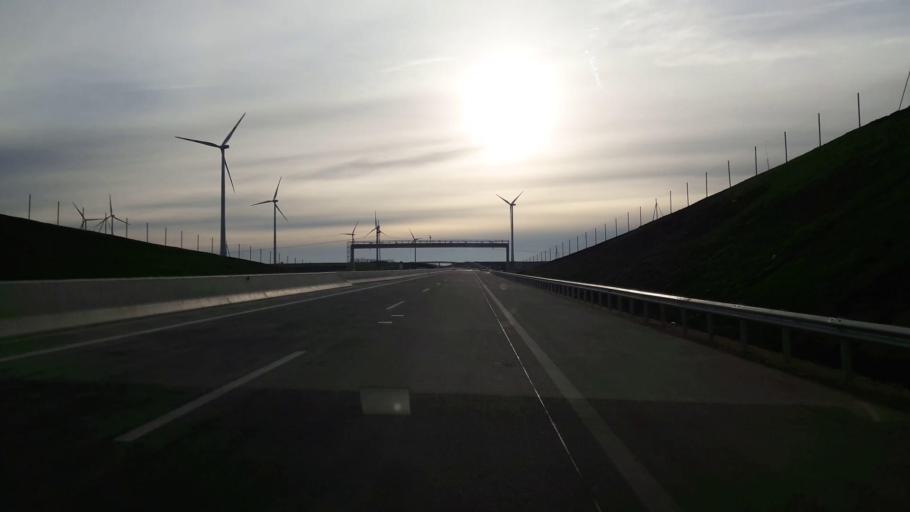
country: AT
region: Lower Austria
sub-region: Politischer Bezirk Mistelbach
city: Grosskrut
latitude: 48.6389
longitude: 16.6840
